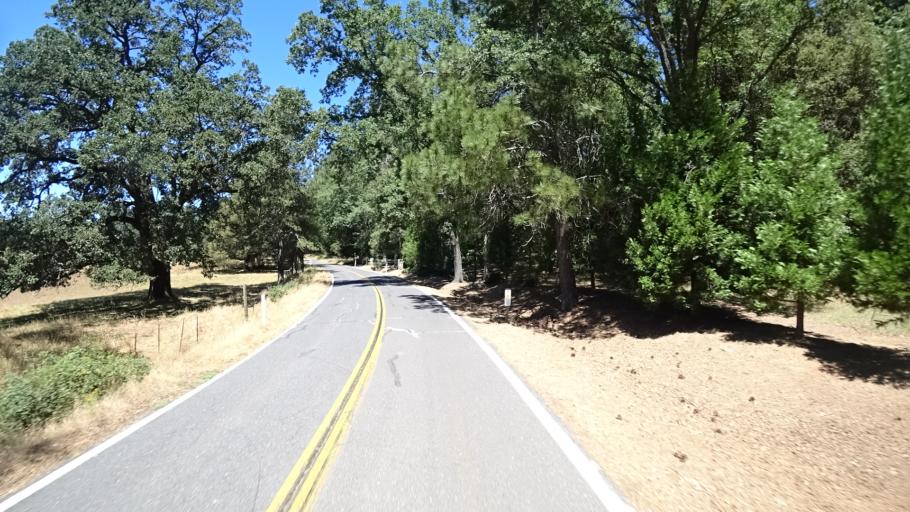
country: US
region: California
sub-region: Amador County
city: Pioneer
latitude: 38.3493
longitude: -120.5586
